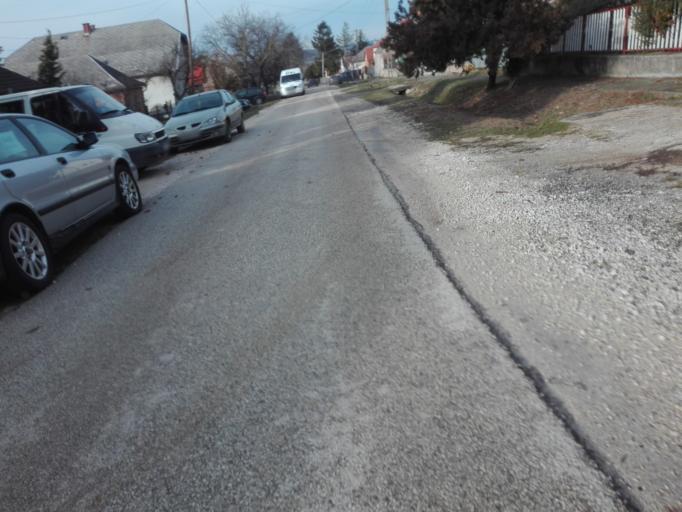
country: HU
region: Veszprem
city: Balatonfured
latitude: 47.0078
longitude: 17.7959
